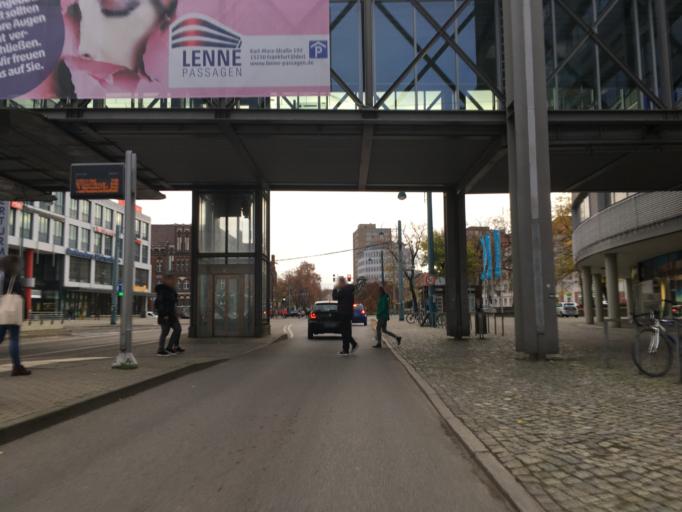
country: DE
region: Brandenburg
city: Frankfurt (Oder)
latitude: 52.3429
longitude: 14.5511
